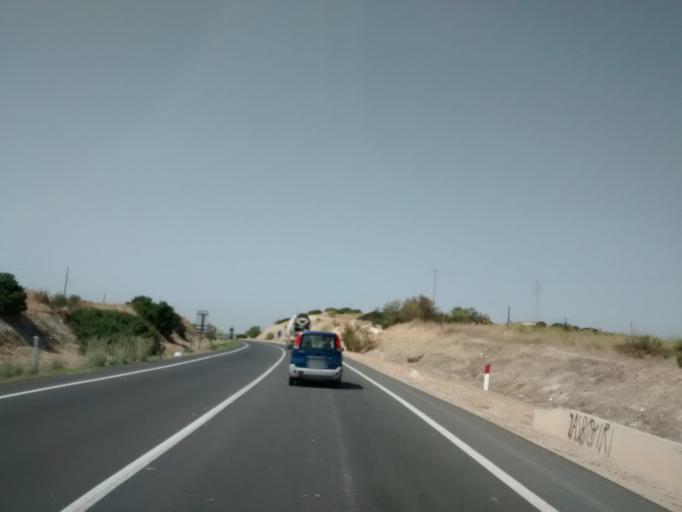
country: IT
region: Sardinia
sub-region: Provincia di Cagliari
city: Maracalagonis
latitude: 39.2684
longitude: 9.2140
